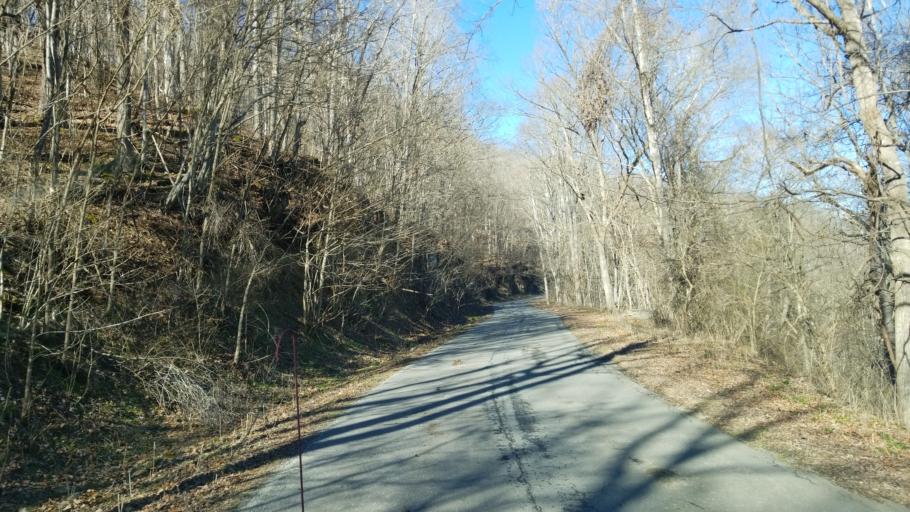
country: US
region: Virginia
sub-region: Pulaski County
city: Pulaski
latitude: 37.1652
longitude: -80.8598
